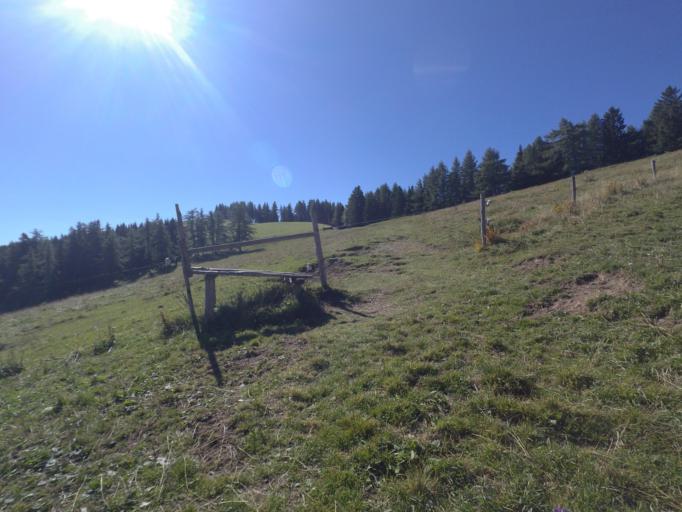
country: AT
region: Styria
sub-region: Politischer Bezirk Weiz
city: Passail
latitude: 47.3370
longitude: 15.4646
